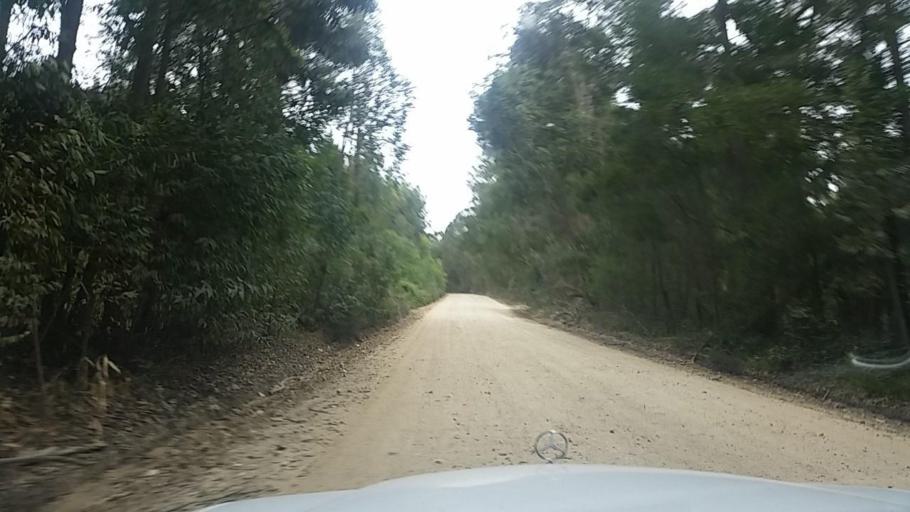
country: ZA
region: Western Cape
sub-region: Eden District Municipality
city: Knysna
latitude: -33.9952
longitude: 23.1370
